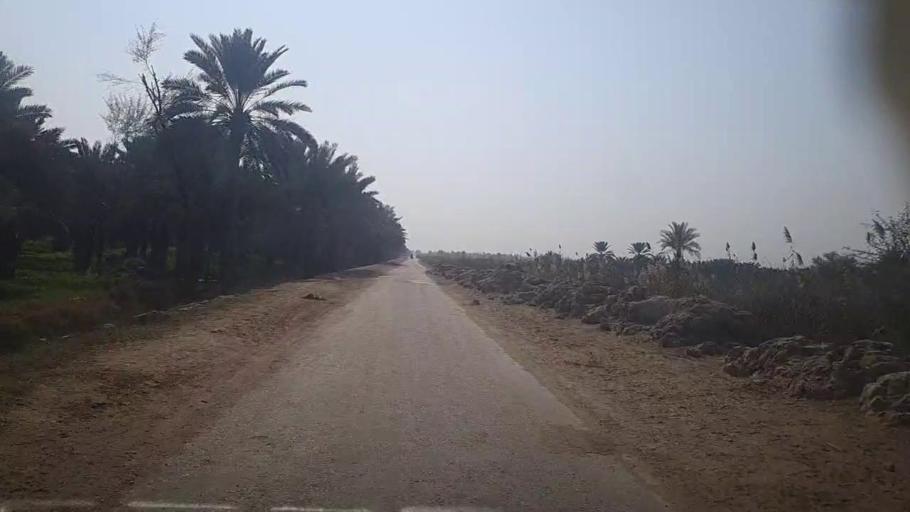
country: PK
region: Sindh
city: Khairpur
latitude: 27.4505
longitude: 68.8117
